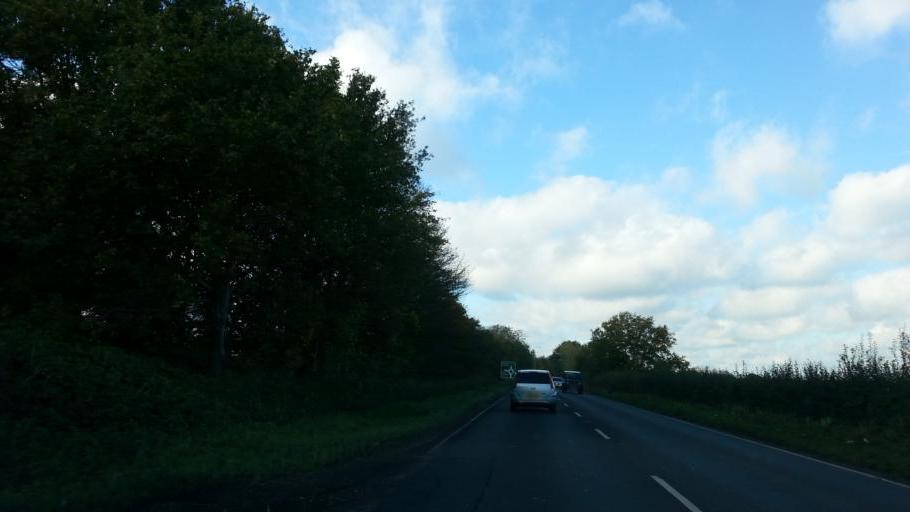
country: GB
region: England
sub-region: Suffolk
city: Beccles
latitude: 52.4812
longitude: 1.5299
